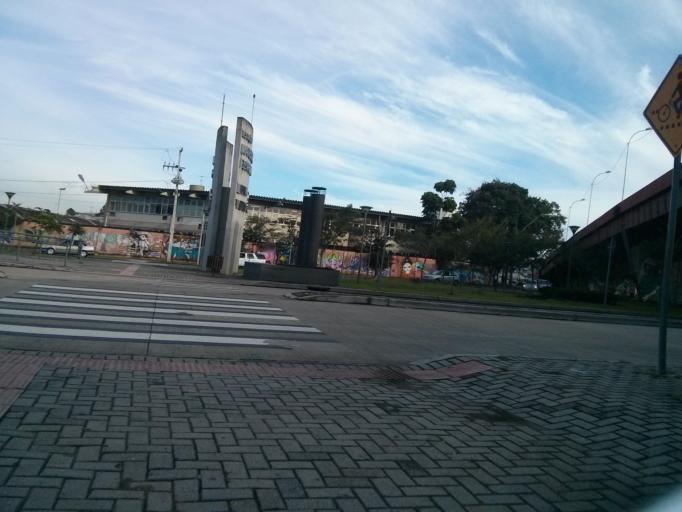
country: BR
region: Parana
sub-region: Curitiba
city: Curitiba
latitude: -25.4690
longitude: -49.2536
